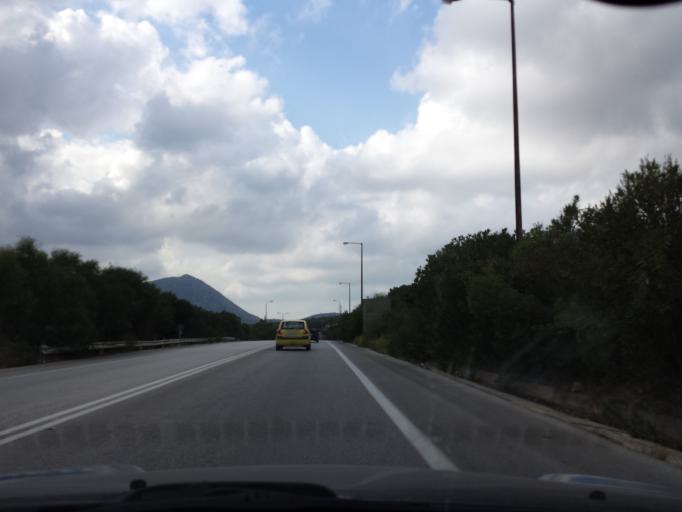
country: GR
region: Crete
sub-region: Nomos Lasithiou
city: Neapoli
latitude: 35.2597
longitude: 25.6113
